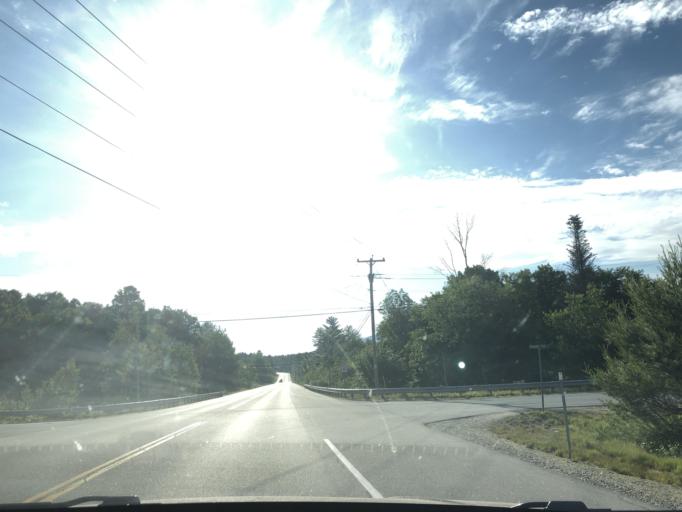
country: US
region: New Hampshire
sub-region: Merrimack County
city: New London
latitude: 43.3932
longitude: -71.9776
